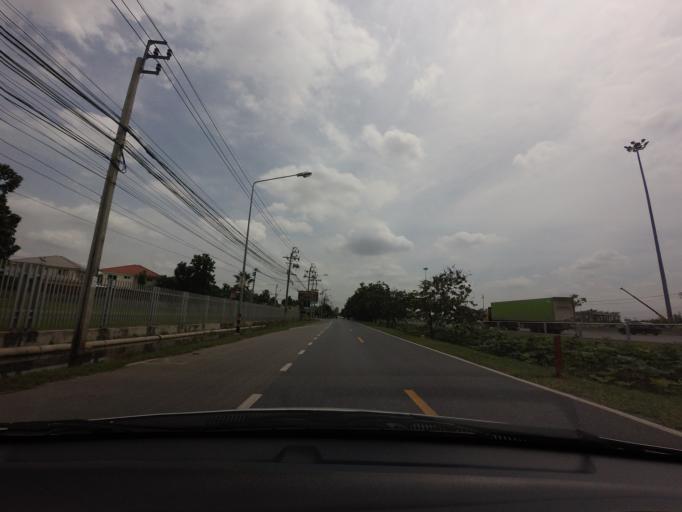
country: TH
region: Bangkok
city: Khan Na Yao
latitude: 13.8629
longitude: 100.6772
